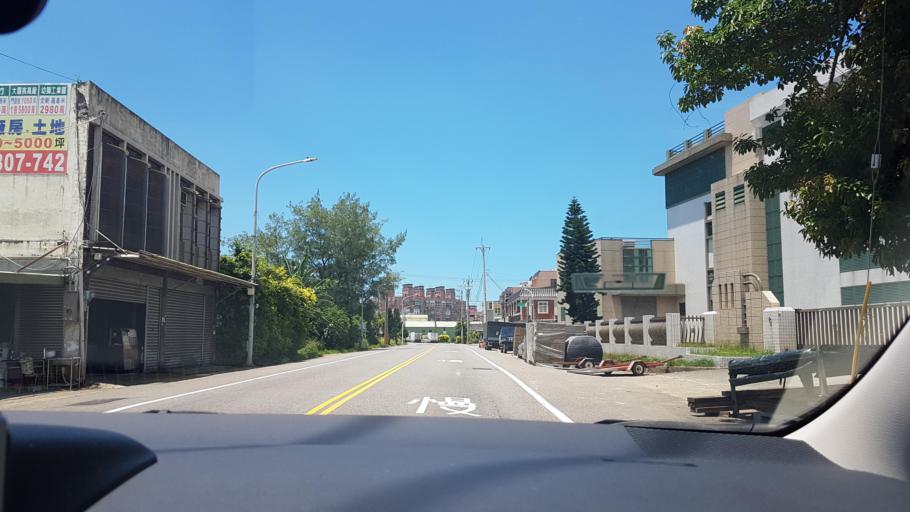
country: TW
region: Taiwan
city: Taoyuan City
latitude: 25.0972
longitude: 121.2634
